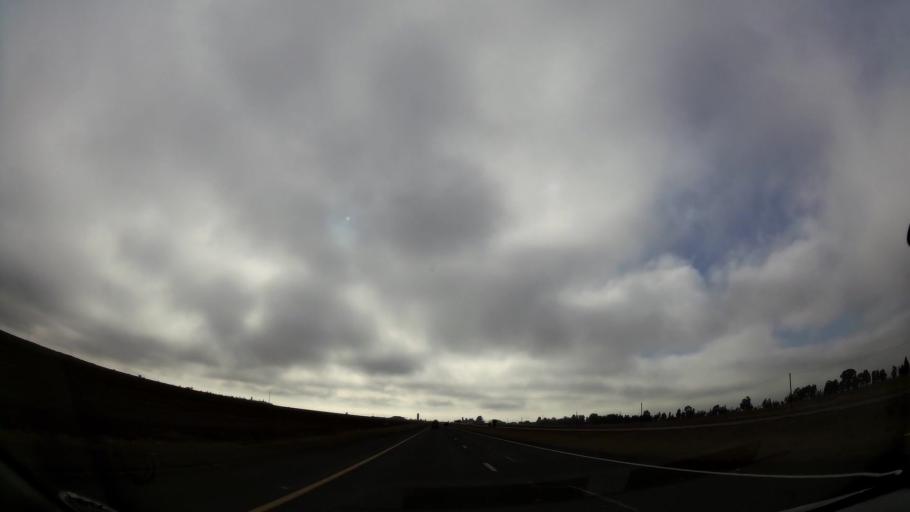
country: ZA
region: Mpumalanga
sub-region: Nkangala District Municipality
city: Delmas
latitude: -26.0491
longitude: 28.8240
